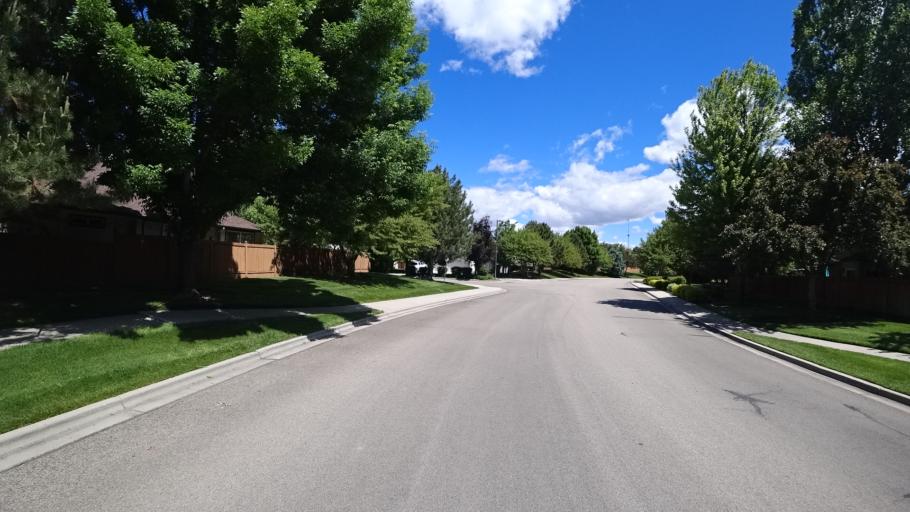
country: US
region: Idaho
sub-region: Ada County
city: Meridian
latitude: 43.6424
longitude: -116.3484
